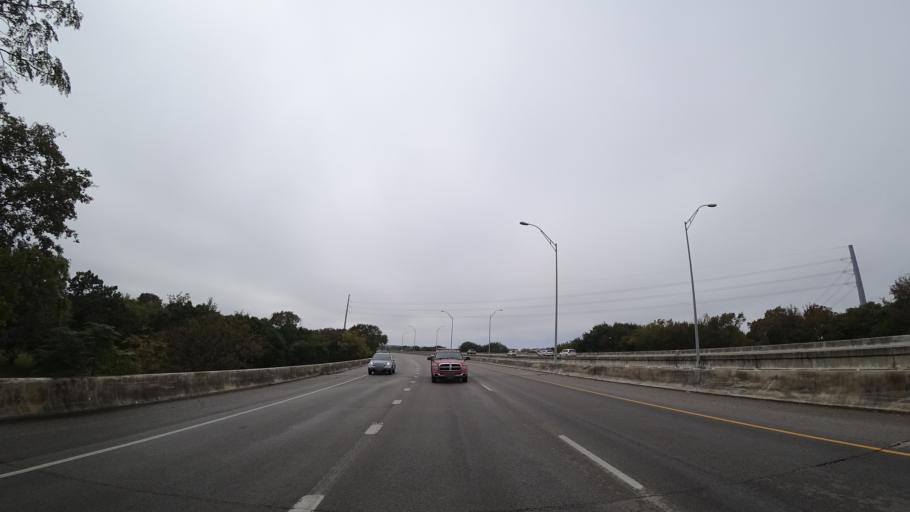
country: US
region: Texas
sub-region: Travis County
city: Shady Hollow
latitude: 30.2164
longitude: -97.8502
